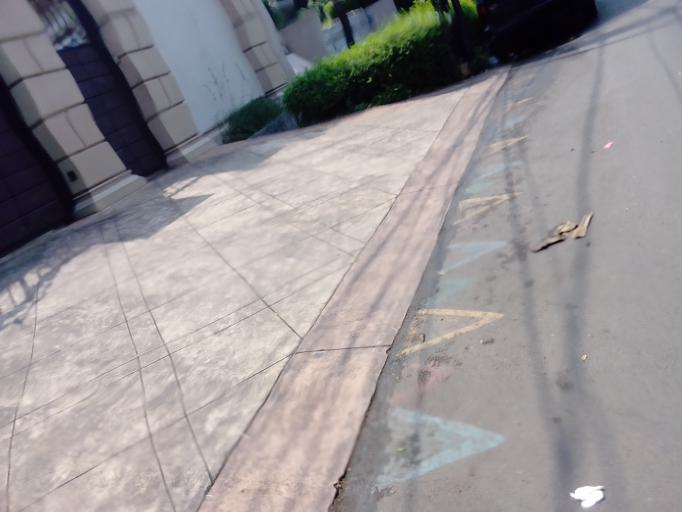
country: ID
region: Jakarta Raya
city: Jakarta
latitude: -6.2280
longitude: 106.7938
